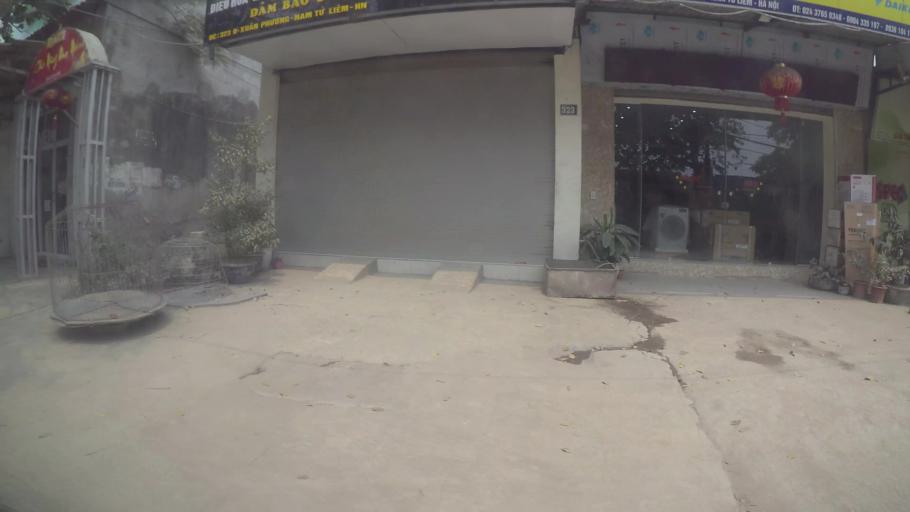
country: VN
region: Ha Noi
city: Cau Dien
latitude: 21.0322
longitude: 105.7391
